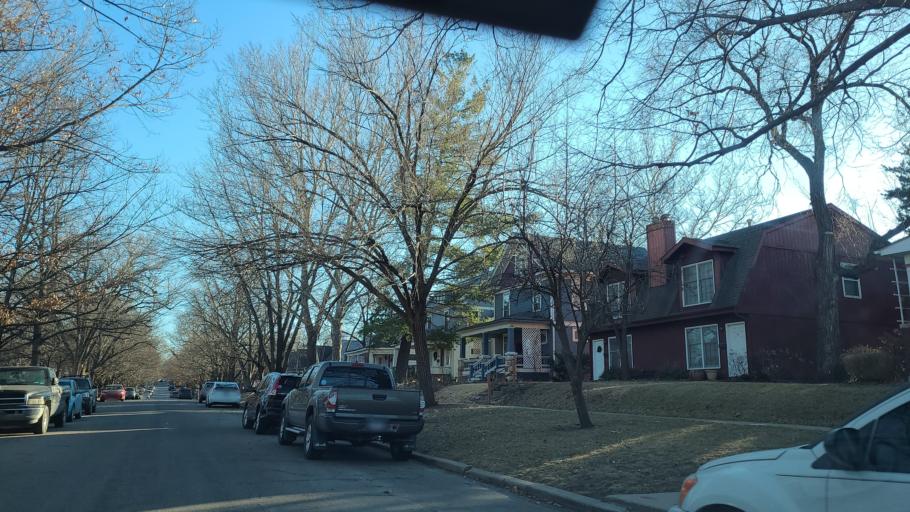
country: US
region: Kansas
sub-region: Douglas County
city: Lawrence
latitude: 38.9710
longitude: -95.2487
